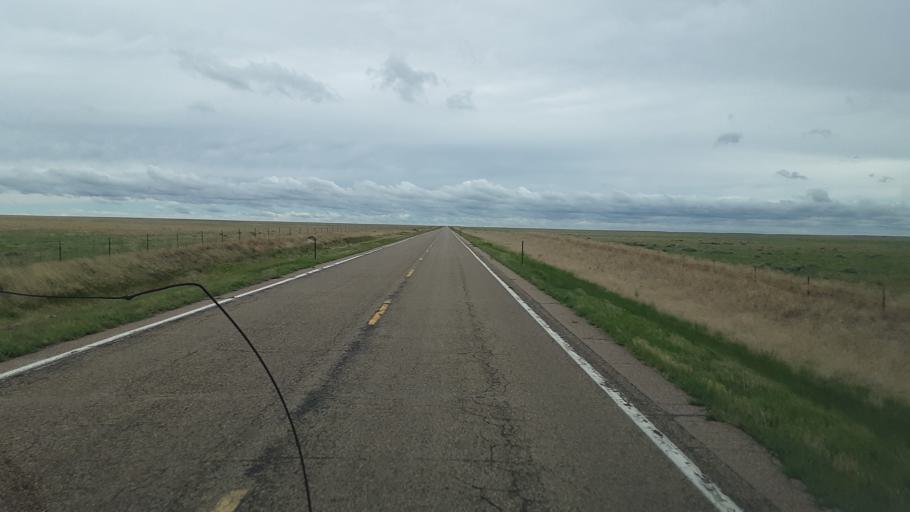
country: US
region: Colorado
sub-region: Lincoln County
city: Hugo
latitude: 38.8521
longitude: -103.7384
